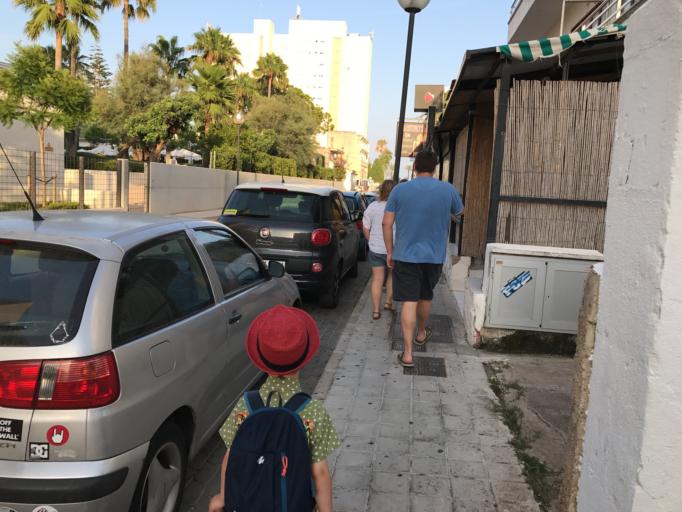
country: ES
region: Balearic Islands
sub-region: Illes Balears
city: Son Servera
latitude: 39.5966
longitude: 3.3810
